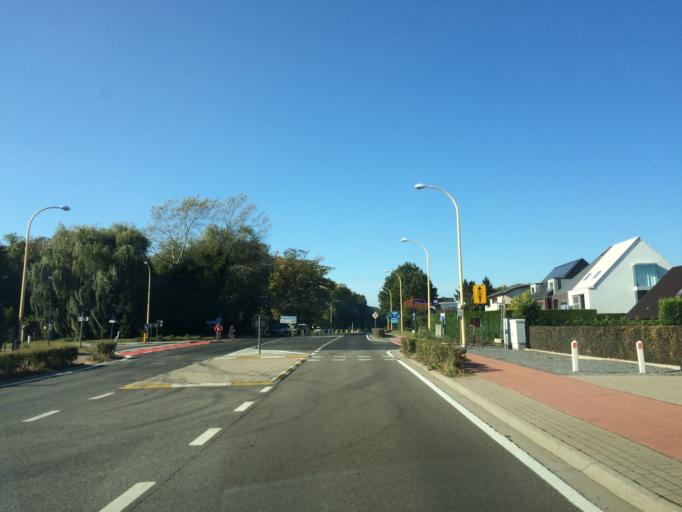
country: BE
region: Flanders
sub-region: Provincie Vlaams-Brabant
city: Meise
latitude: 50.9438
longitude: 4.3294
